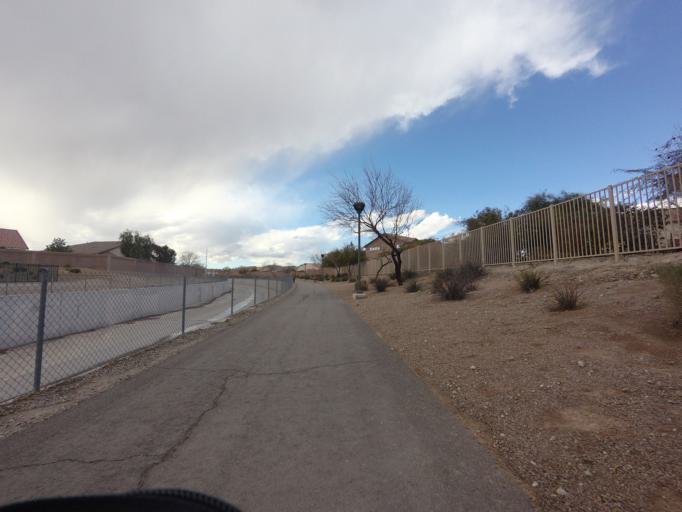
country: US
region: Nevada
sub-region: Clark County
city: North Las Vegas
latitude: 36.2630
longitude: -115.1863
